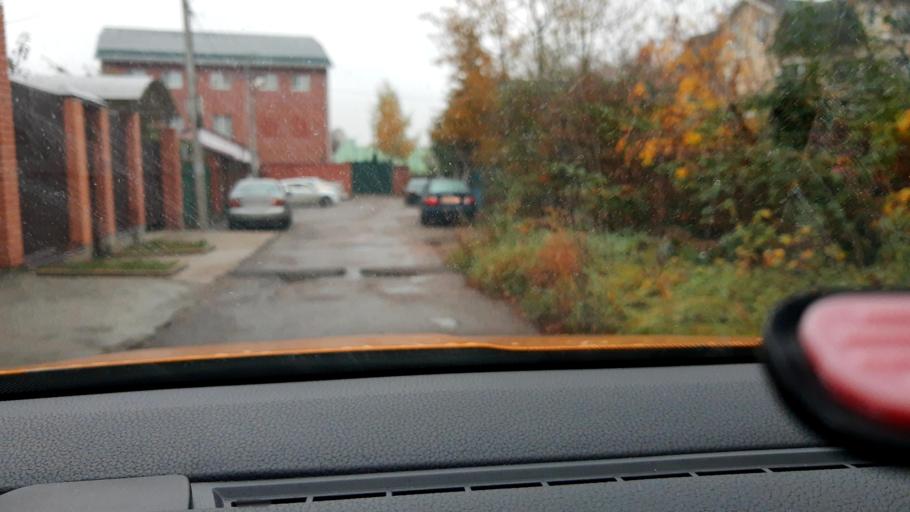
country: RU
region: Moskovskaya
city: Marfino
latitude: 55.7038
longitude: 37.3869
